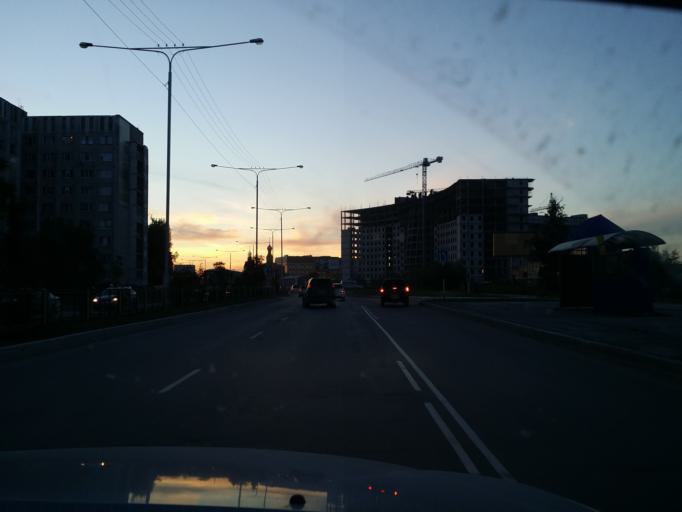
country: RU
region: Khanty-Mansiyskiy Avtonomnyy Okrug
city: Nizhnevartovsk
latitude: 60.9456
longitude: 76.5665
